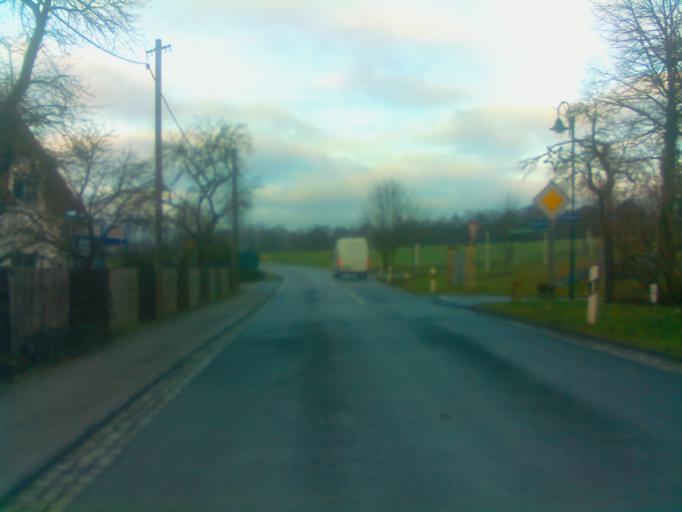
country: DE
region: Thuringia
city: Hummelshain
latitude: 50.7676
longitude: 11.6249
